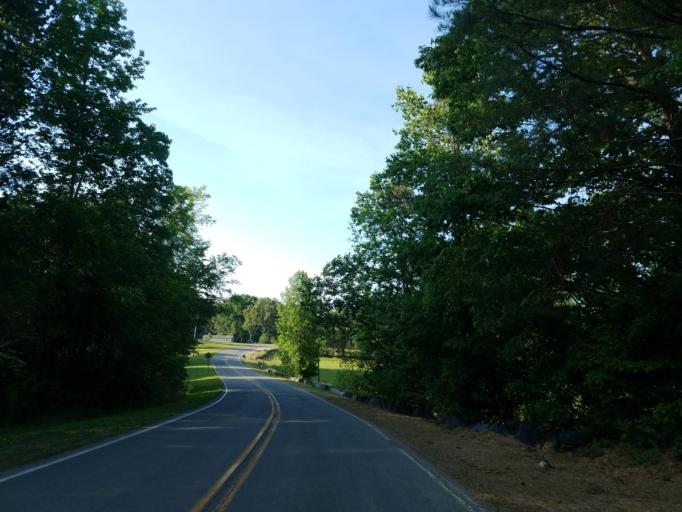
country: US
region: Georgia
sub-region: Floyd County
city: Shannon
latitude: 34.4890
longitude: -85.1279
